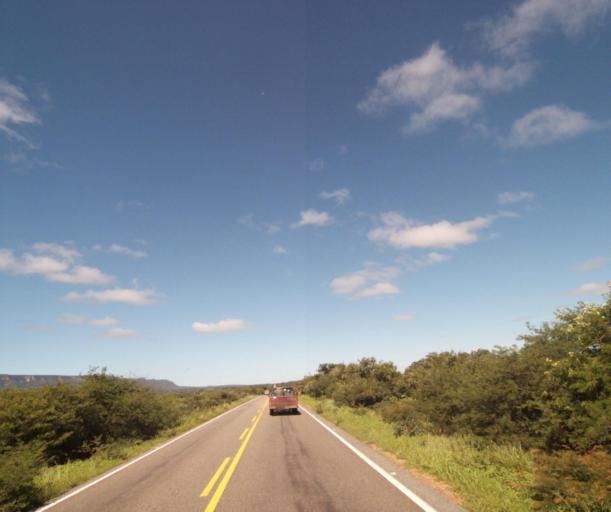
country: BR
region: Bahia
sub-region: Palmas De Monte Alto
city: Palmas de Monte Alto
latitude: -14.2416
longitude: -43.0643
